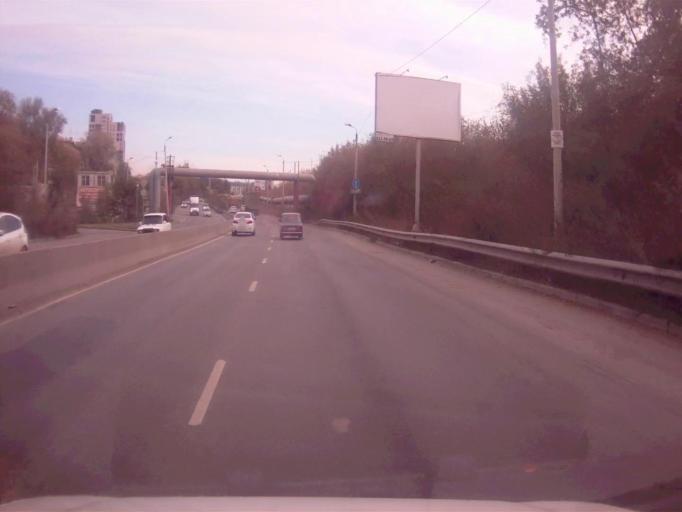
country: RU
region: Chelyabinsk
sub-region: Gorod Chelyabinsk
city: Chelyabinsk
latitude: 55.1592
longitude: 61.4320
